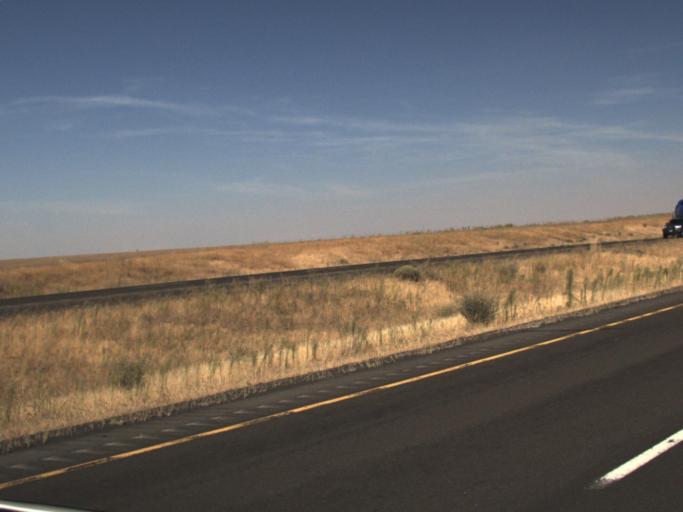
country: US
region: Washington
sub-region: Adams County
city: Ritzville
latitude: 47.1847
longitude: -118.2677
